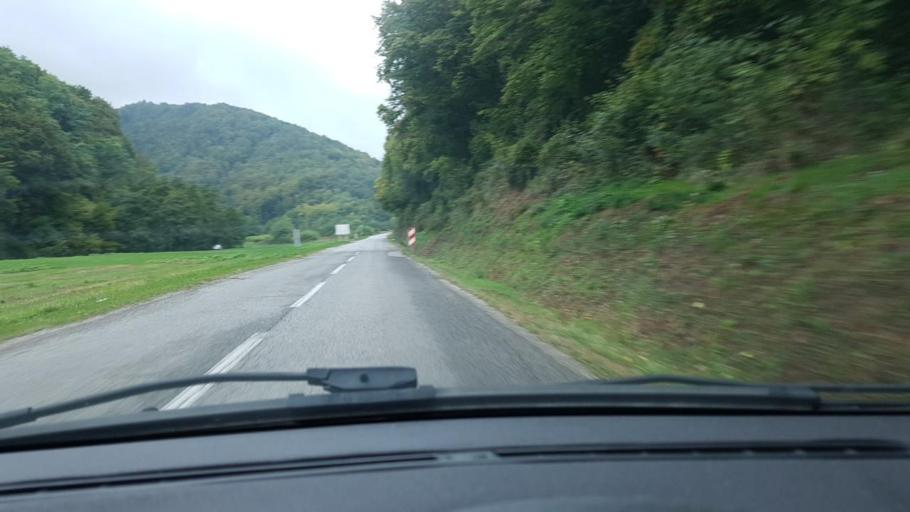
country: HR
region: Krapinsko-Zagorska
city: Marija Bistrica
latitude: 45.9307
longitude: 16.1158
